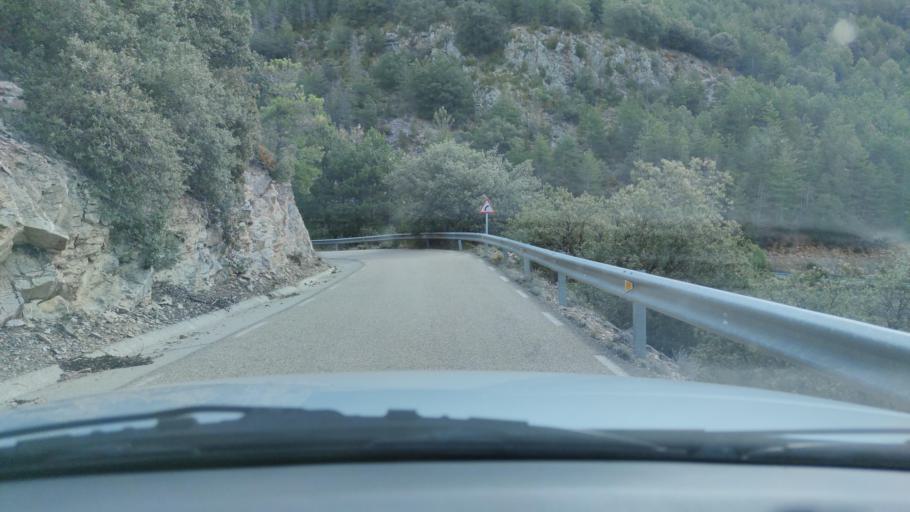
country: ES
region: Catalonia
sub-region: Provincia de Lleida
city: la Seu d'Urgell
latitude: 42.2507
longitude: 1.4136
